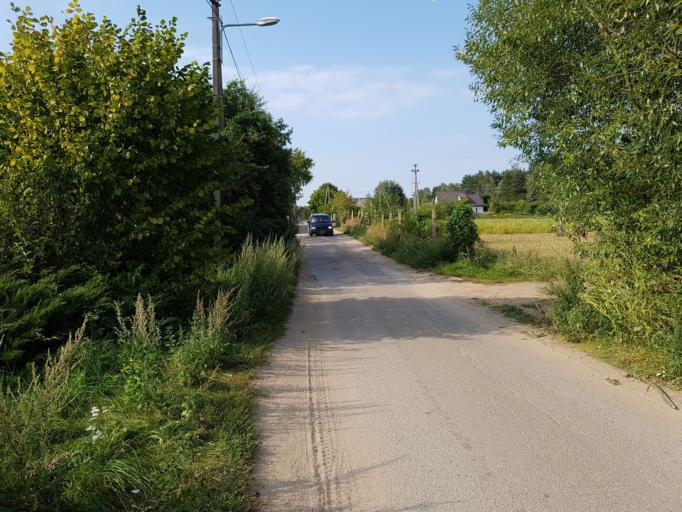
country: LT
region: Vilnius County
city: Rasos
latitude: 54.7896
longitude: 25.3656
